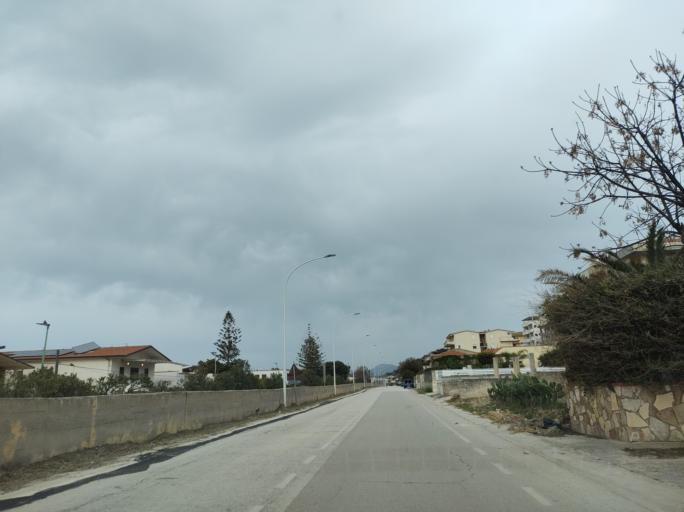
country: IT
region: Sicily
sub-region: Trapani
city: Alcamo
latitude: 38.0256
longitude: 12.9233
